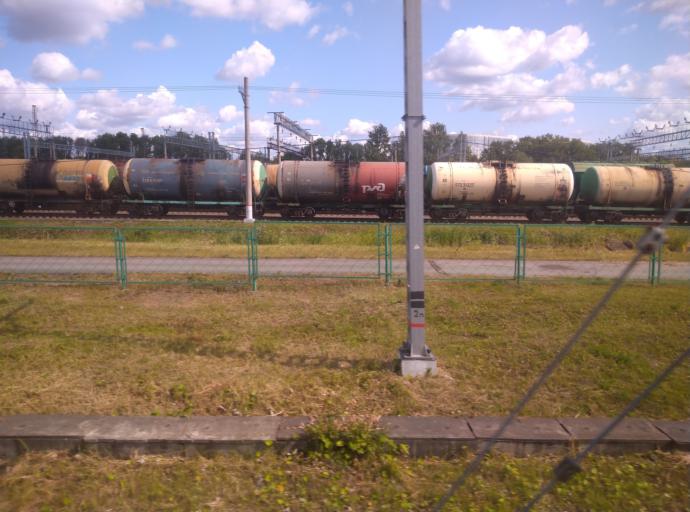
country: RU
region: St.-Petersburg
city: Obukhovo
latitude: 59.8581
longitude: 30.4390
